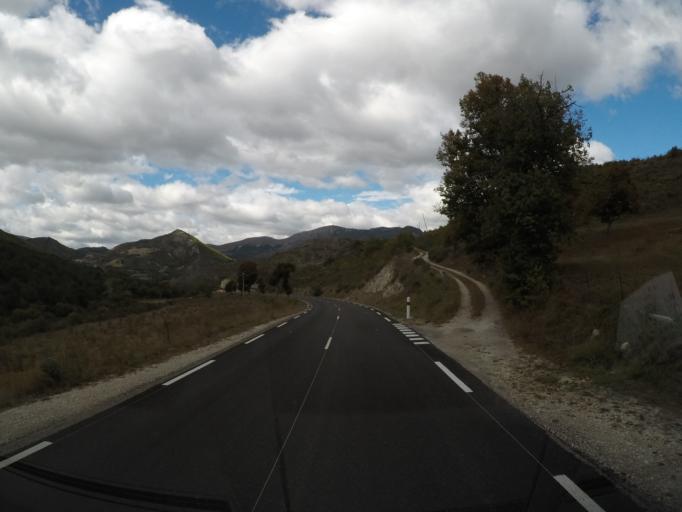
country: FR
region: Provence-Alpes-Cote d'Azur
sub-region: Departement du Vaucluse
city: Sault
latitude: 44.1843
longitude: 5.5546
